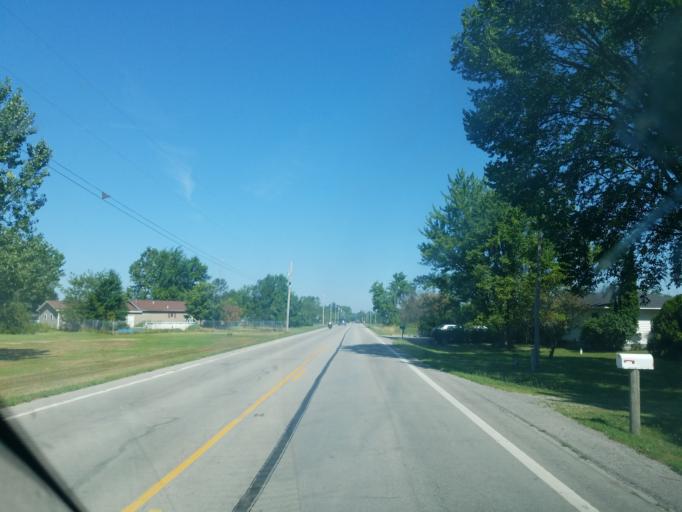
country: US
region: Ohio
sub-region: Logan County
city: Russells Point
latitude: 40.4653
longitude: -83.8327
